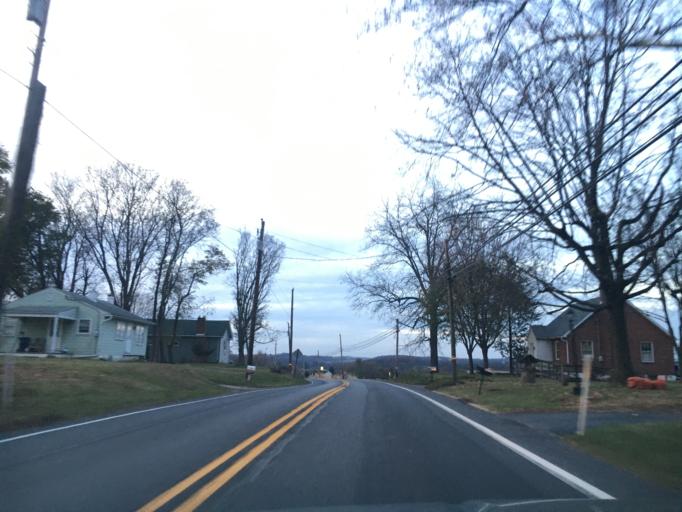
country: US
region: Pennsylvania
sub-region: Lehigh County
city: Egypt
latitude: 40.6509
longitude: -75.5391
